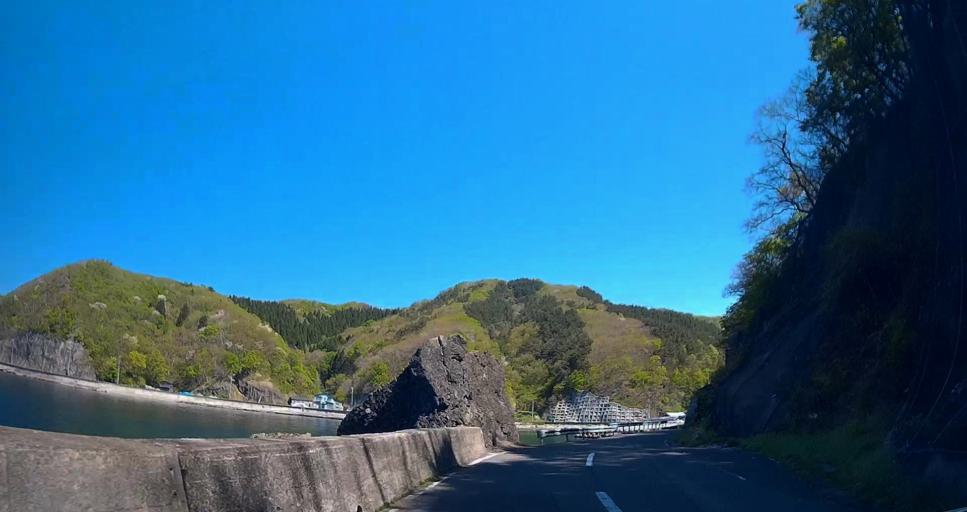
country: JP
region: Aomori
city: Aomori Shi
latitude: 41.1367
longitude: 140.7782
